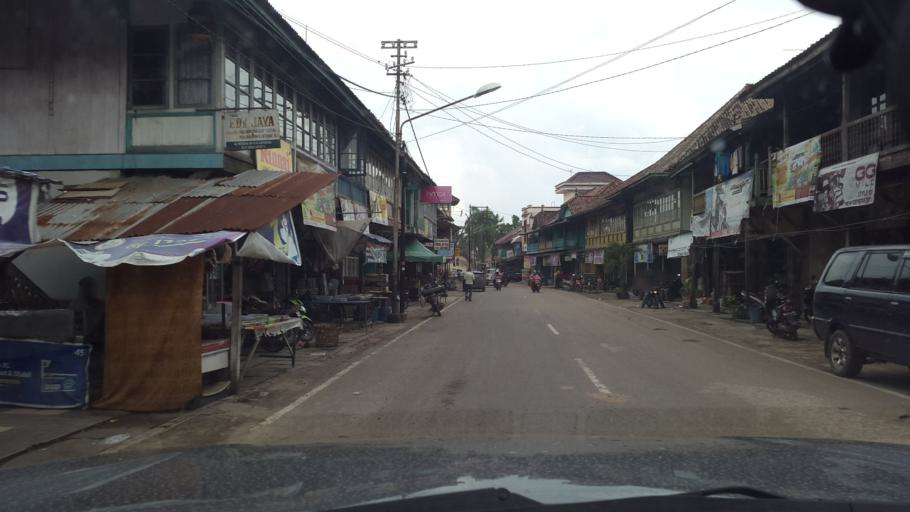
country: ID
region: South Sumatra
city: Kayu Agung
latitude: -3.3909
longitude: 104.8321
